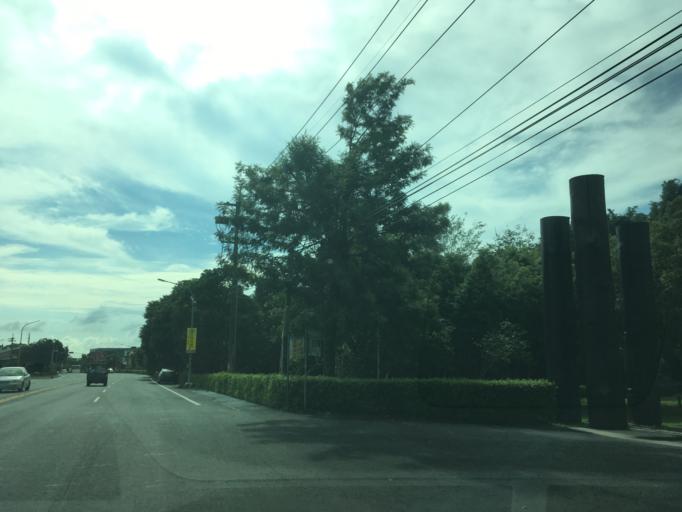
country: TW
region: Taiwan
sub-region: Chiayi
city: Jiayi Shi
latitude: 23.4529
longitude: 120.5587
